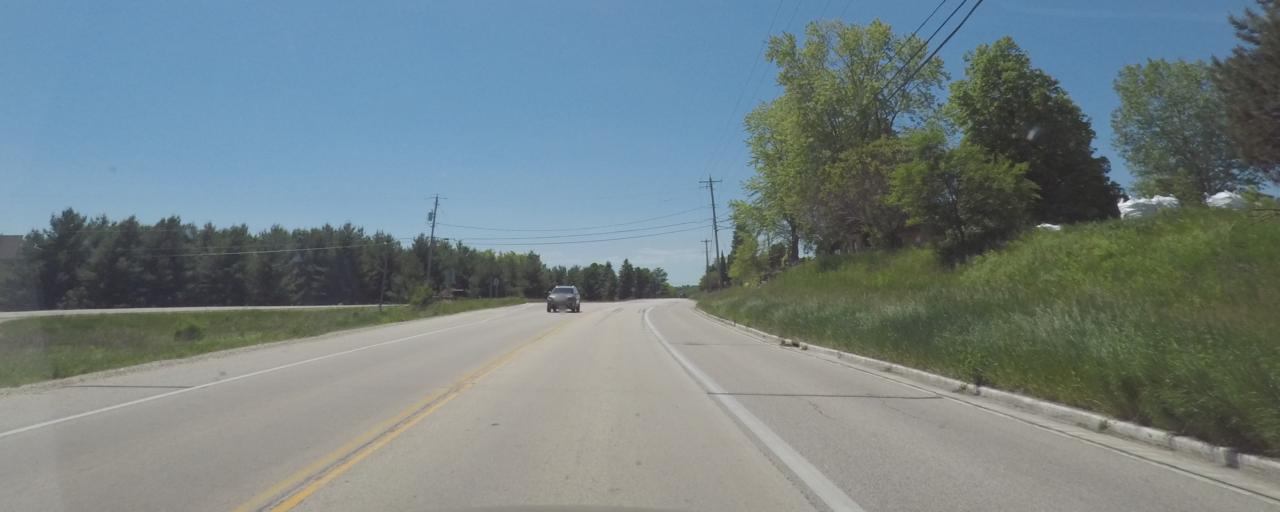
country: US
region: Wisconsin
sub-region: Washington County
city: West Bend
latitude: 43.4557
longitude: -88.1619
